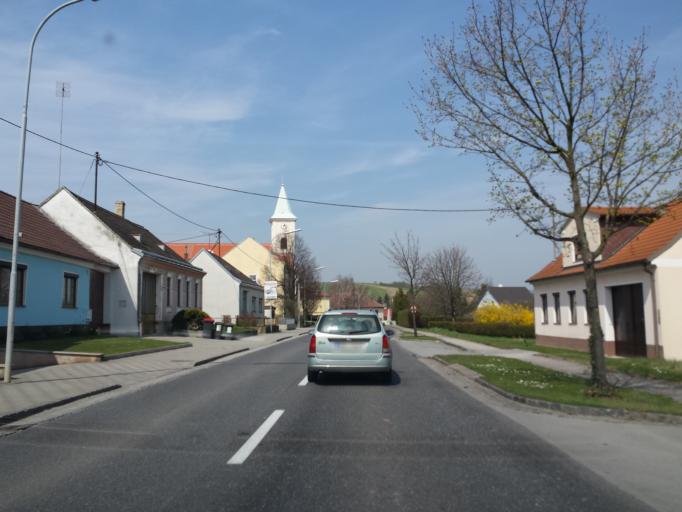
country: AT
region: Lower Austria
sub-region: Politischer Bezirk Mistelbach
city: Wilfersdorf
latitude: 48.6236
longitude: 16.6463
